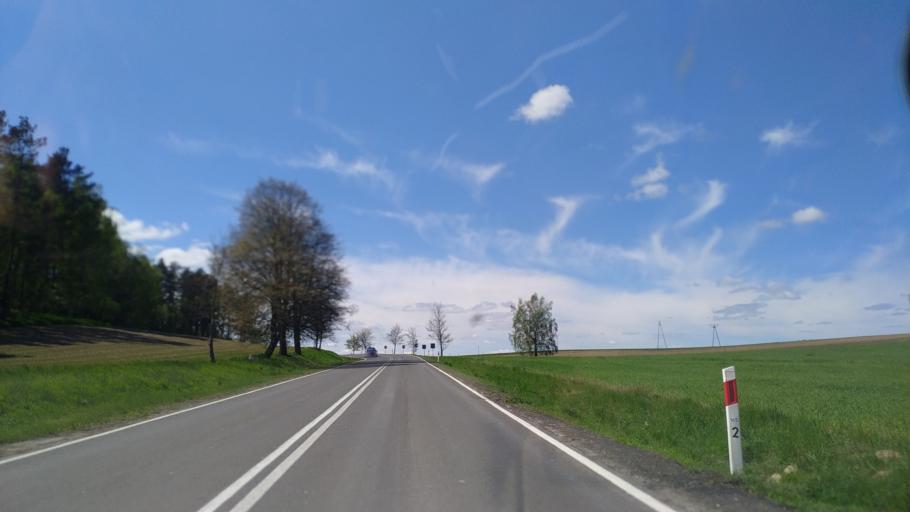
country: PL
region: Greater Poland Voivodeship
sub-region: Powiat pilski
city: Szydlowo
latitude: 53.2408
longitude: 16.6359
